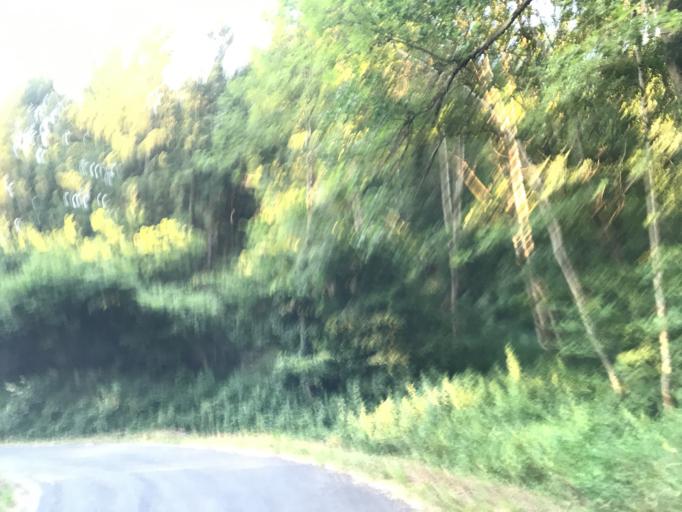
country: FR
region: Auvergne
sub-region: Departement du Puy-de-Dome
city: Courpiere
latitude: 45.7530
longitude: 3.6202
